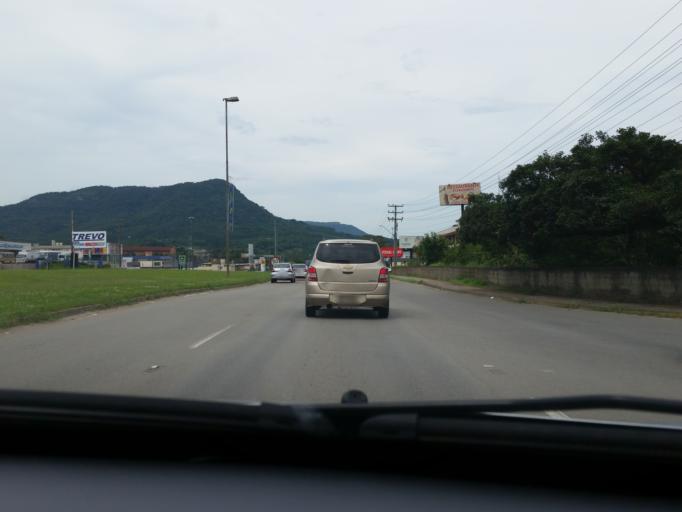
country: BR
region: Santa Catarina
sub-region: Rio Do Sul
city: Rio do Sul
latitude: -27.2007
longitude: -49.6317
